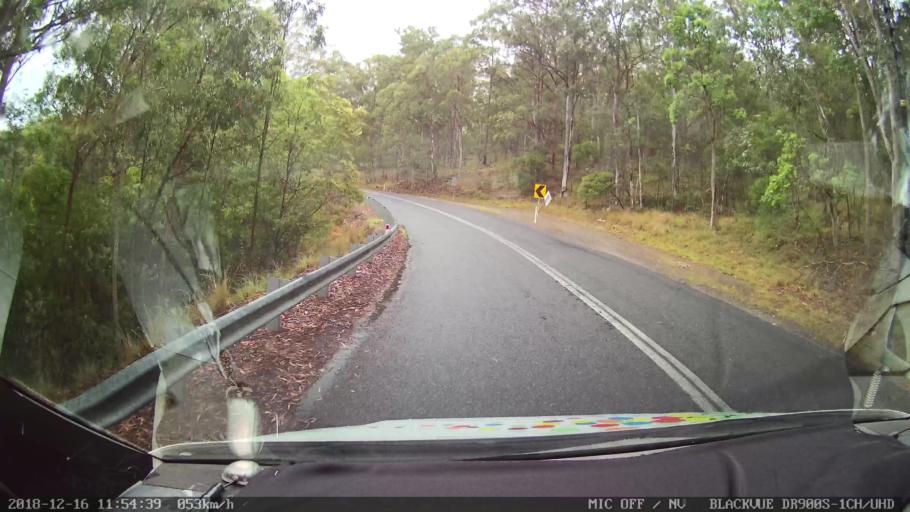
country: AU
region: New South Wales
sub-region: Tenterfield Municipality
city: Carrolls Creek
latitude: -28.9100
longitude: 152.2861
